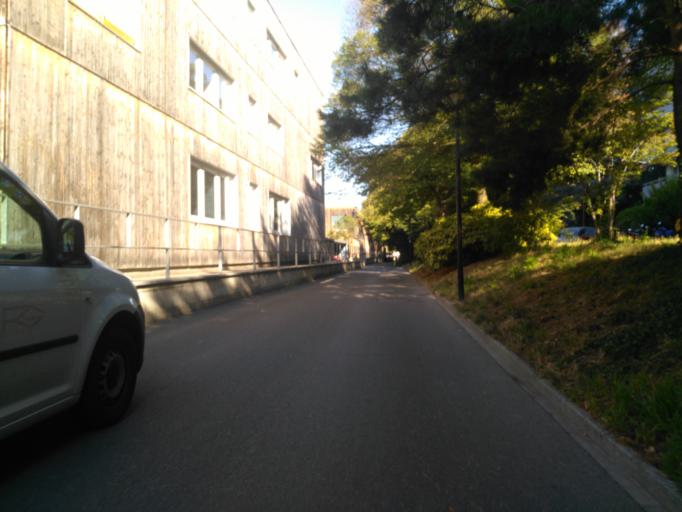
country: CH
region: Geneva
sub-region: Geneva
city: Lancy
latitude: 46.2061
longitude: 6.1260
